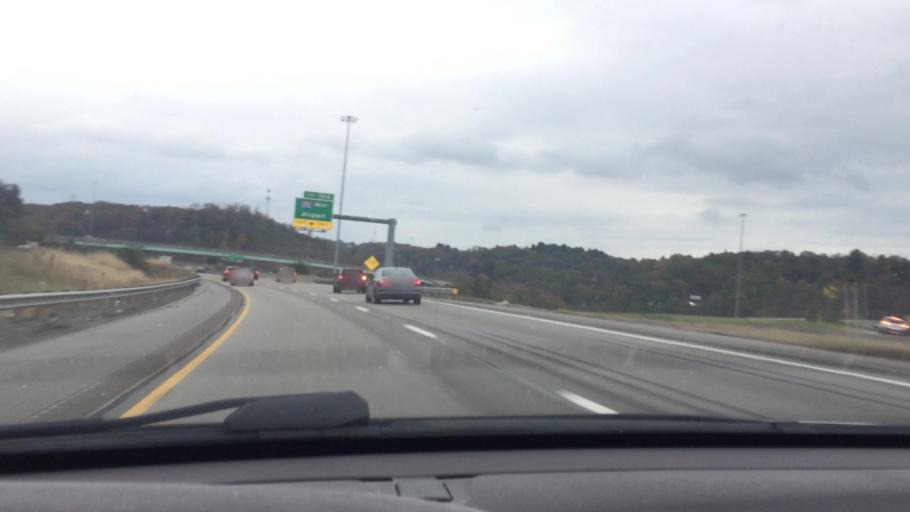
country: US
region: Pennsylvania
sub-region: Allegheny County
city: Carnegie
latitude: 40.4199
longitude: -80.1034
